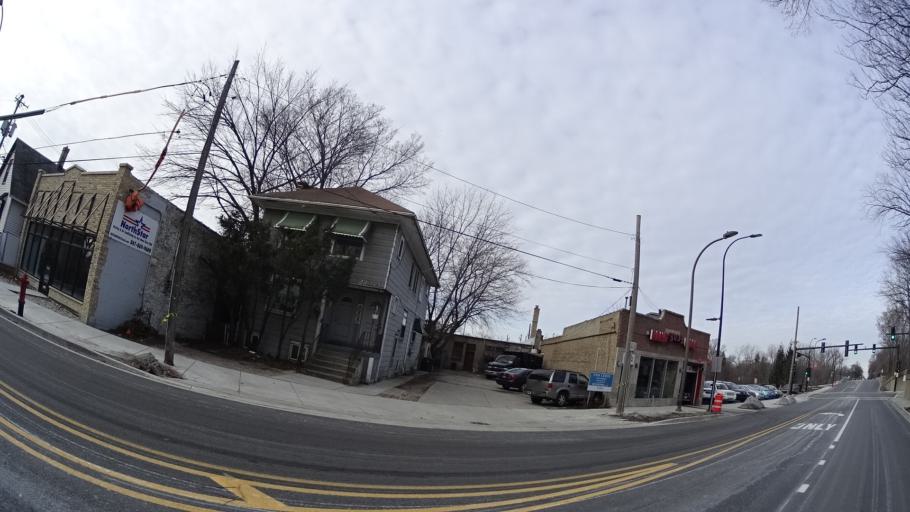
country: US
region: Illinois
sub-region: Cook County
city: Evanston
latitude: 42.0579
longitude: -87.6933
